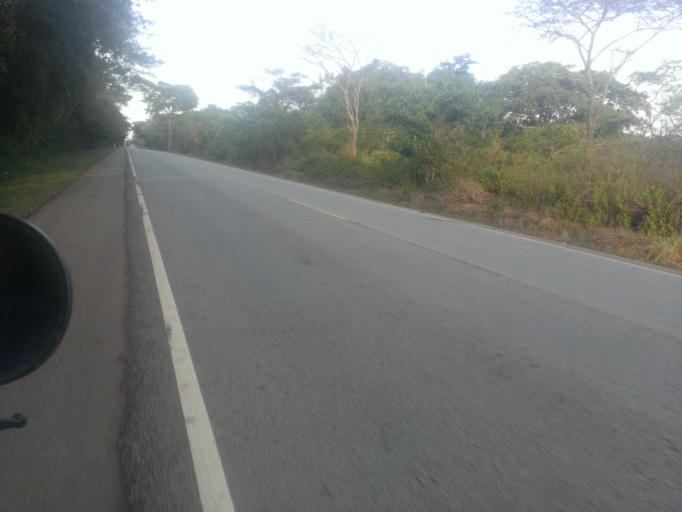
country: UG
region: Eastern Region
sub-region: Busia District
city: Busia
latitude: 0.5307
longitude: 33.9839
